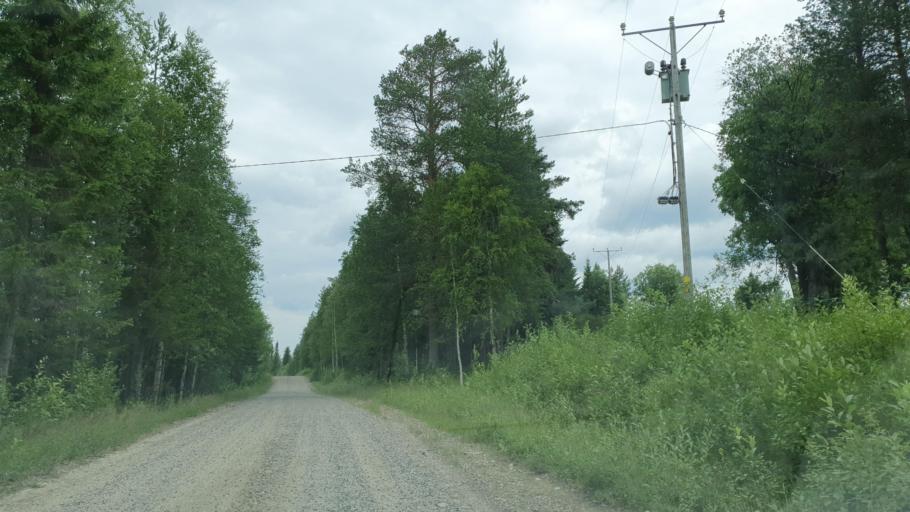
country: FI
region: Kainuu
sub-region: Kehys-Kainuu
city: Kuhmo
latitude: 64.7318
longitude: 29.6369
